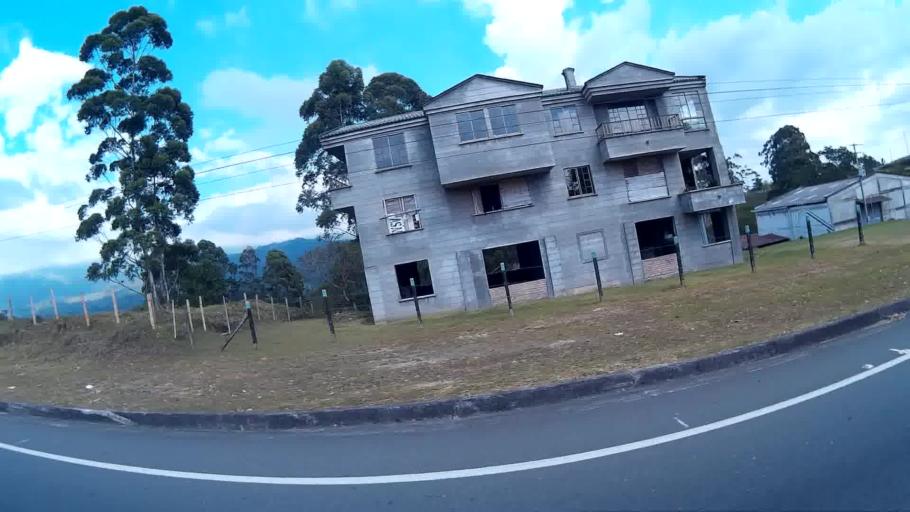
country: CO
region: Quindio
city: Circasia
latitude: 4.6082
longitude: -75.6344
